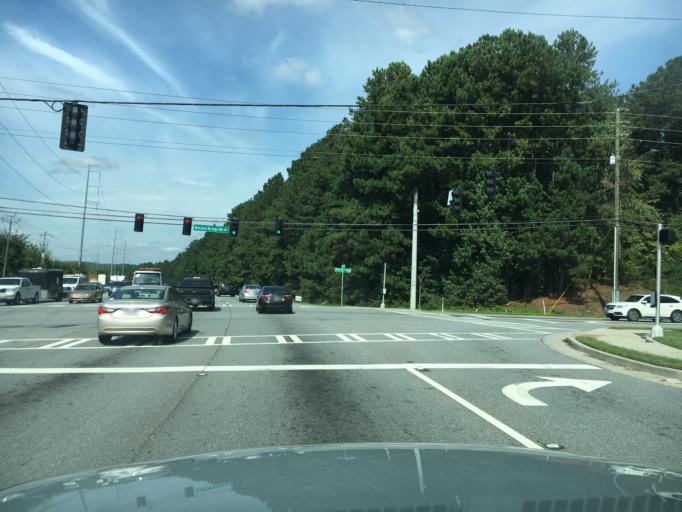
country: US
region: Georgia
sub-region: Gwinnett County
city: Duluth
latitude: 34.0019
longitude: -84.1630
